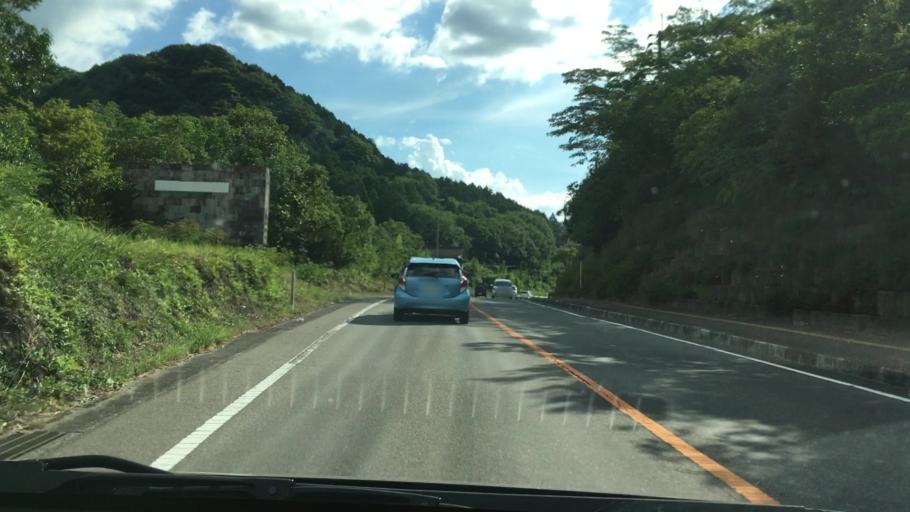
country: JP
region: Saga Prefecture
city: Imaricho-ko
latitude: 33.1884
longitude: 129.8596
